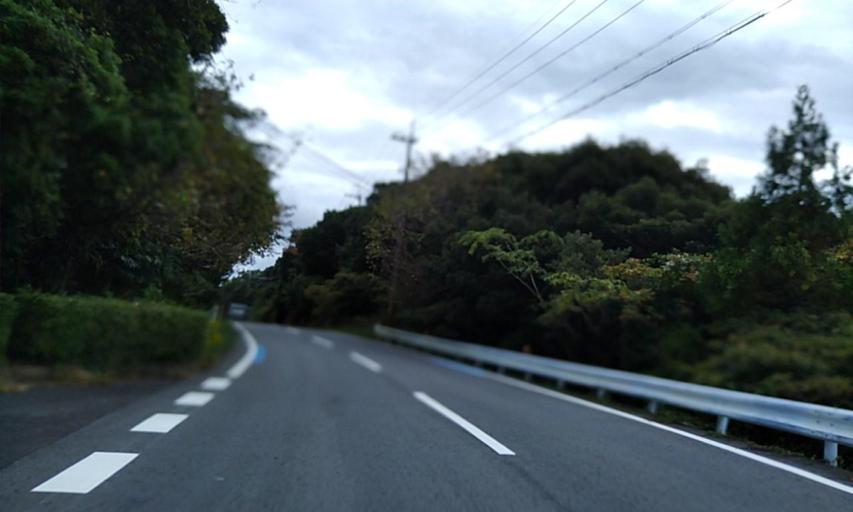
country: JP
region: Wakayama
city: Shingu
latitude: 33.4715
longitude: 135.8178
